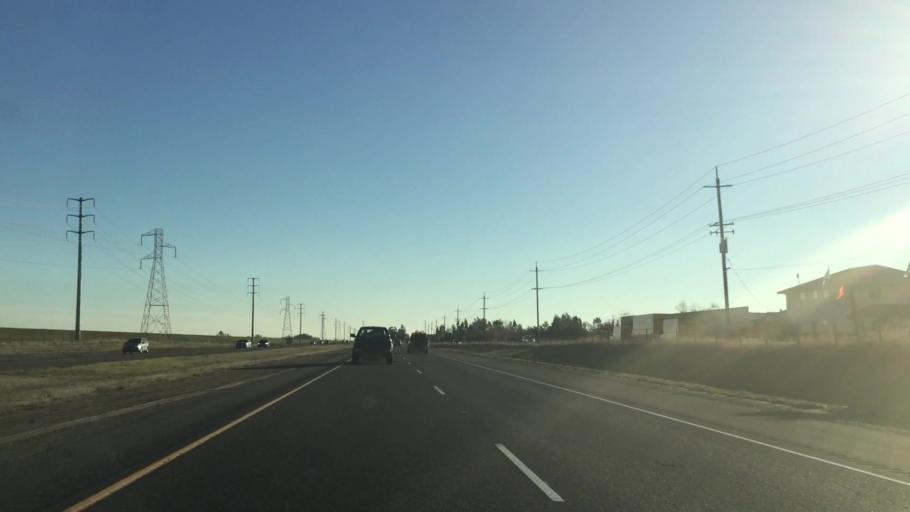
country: US
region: California
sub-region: Yuba County
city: Plumas Lake
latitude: 39.0422
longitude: -121.5433
